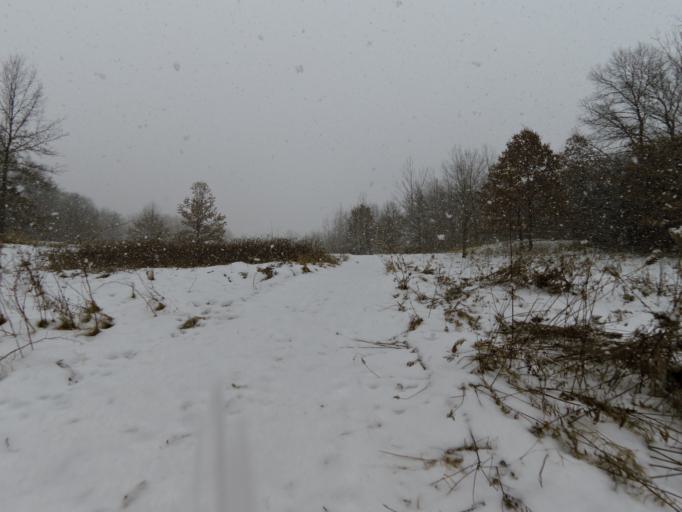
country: US
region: Minnesota
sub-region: Washington County
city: Lake Elmo
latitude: 44.9789
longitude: -92.9031
